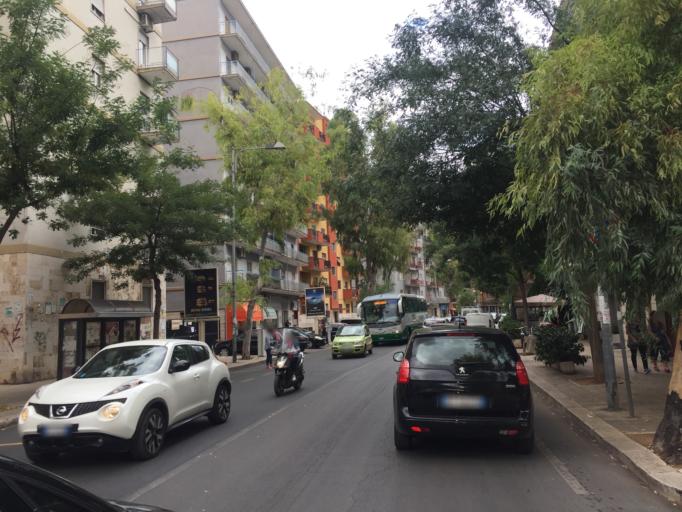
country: IT
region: Apulia
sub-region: Provincia di Bari
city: Bari
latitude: 41.1086
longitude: 16.8602
